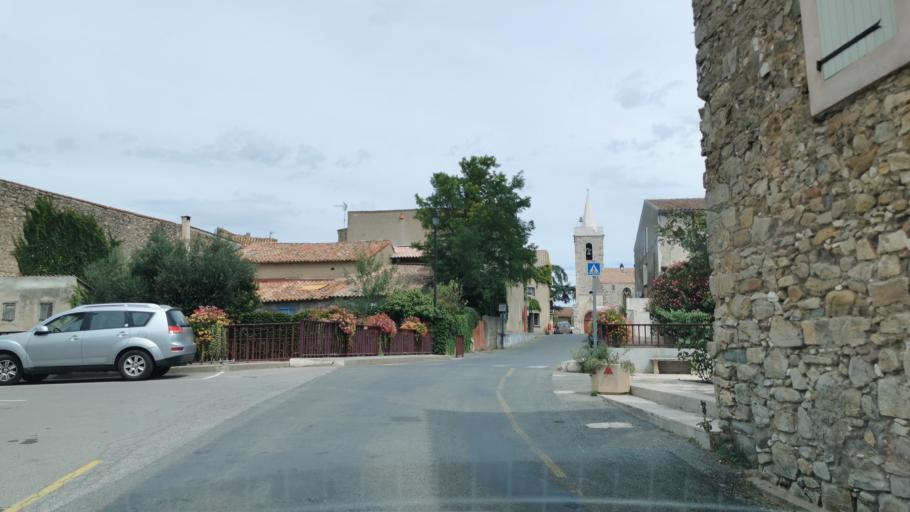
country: FR
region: Languedoc-Roussillon
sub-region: Departement de l'Aude
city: Bize-Minervois
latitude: 43.3029
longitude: 2.8277
